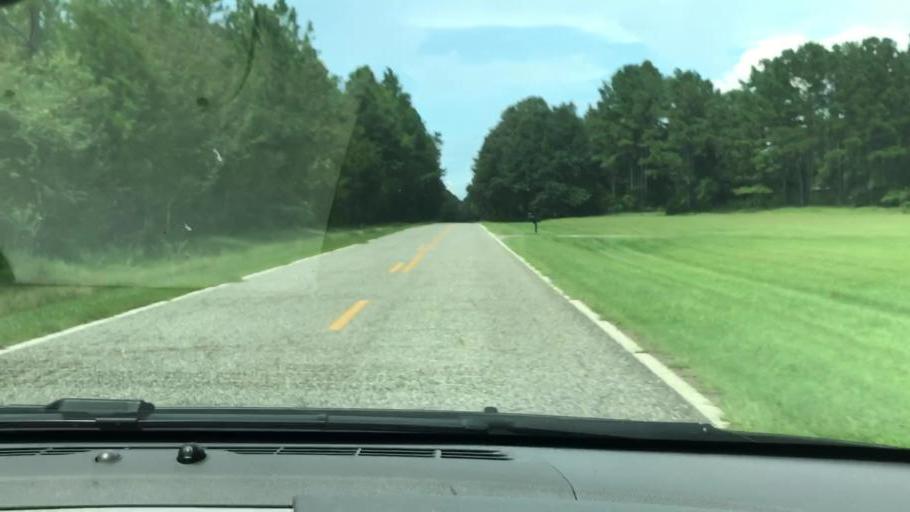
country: US
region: Georgia
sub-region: Seminole County
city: Donalsonville
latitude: 31.1479
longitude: -84.9949
